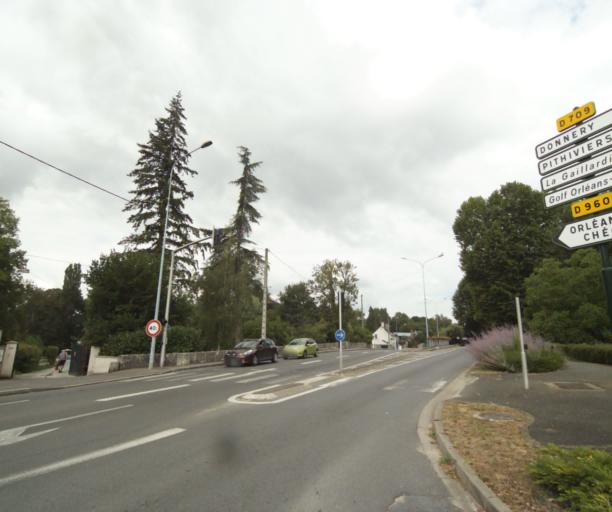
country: FR
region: Centre
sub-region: Departement du Loiret
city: Mardie
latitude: 47.8918
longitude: 2.0533
